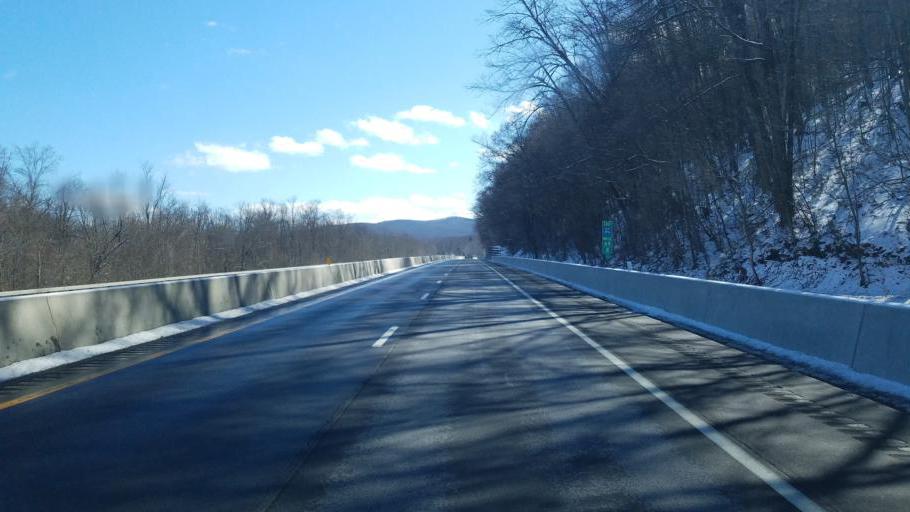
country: US
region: New York
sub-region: Cattaraugus County
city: Salamanca
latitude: 42.1144
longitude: -78.6633
